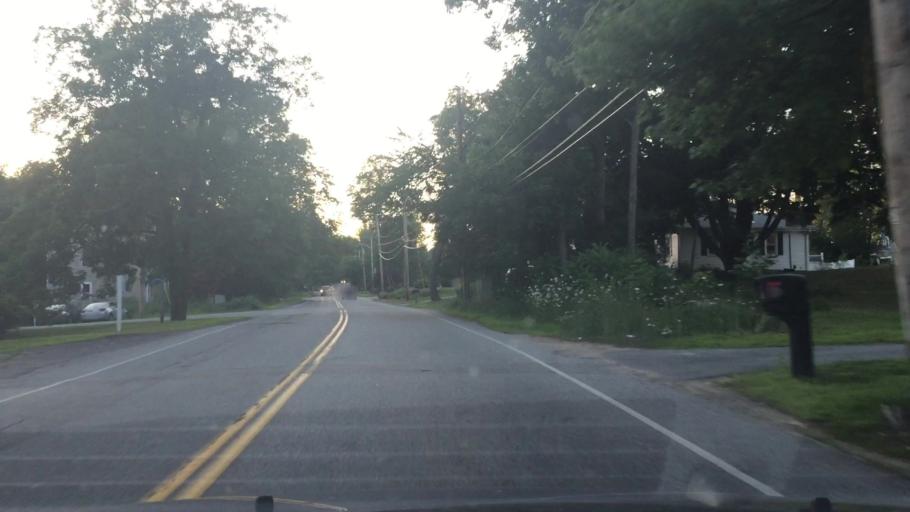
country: US
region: New Hampshire
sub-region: Rockingham County
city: Plaistow
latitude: 42.8103
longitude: -71.0889
